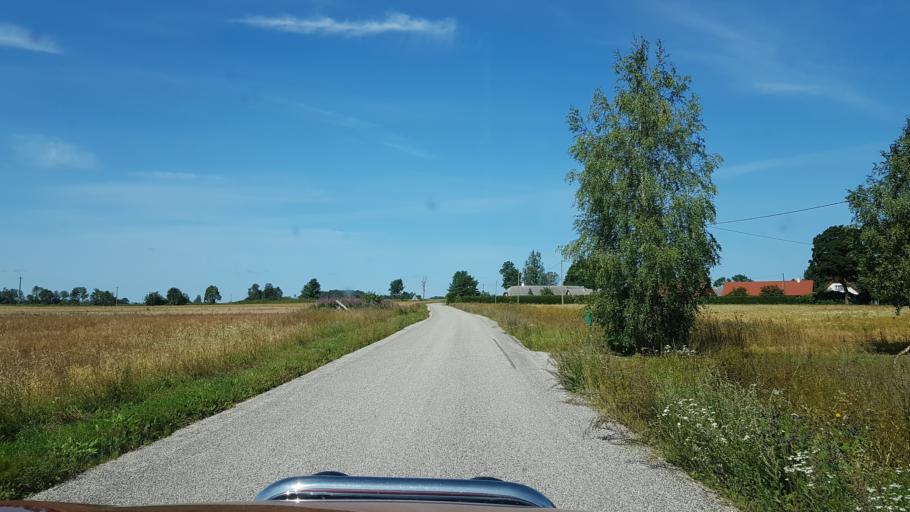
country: EE
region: Jaervamaa
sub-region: Jaerva-Jaani vald
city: Jarva-Jaani
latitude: 59.0841
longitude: 25.7585
